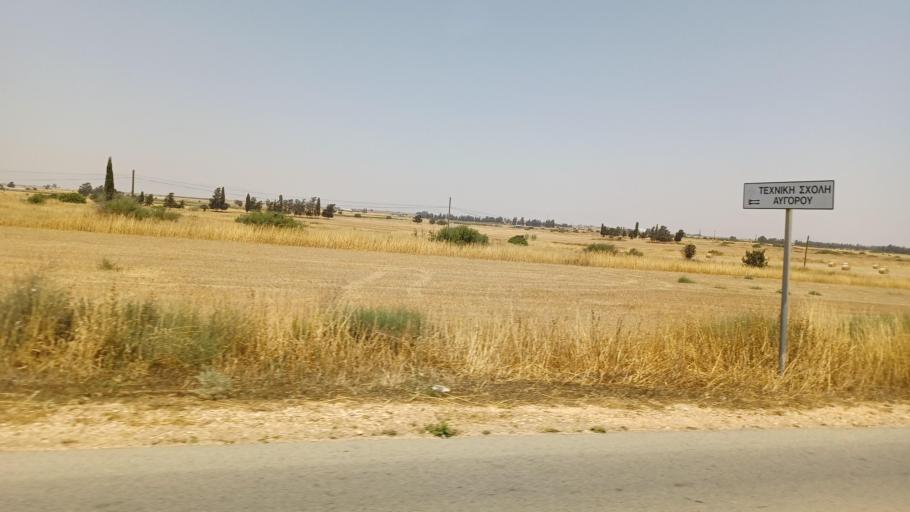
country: CY
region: Ammochostos
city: Achna
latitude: 35.0603
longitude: 33.8017
